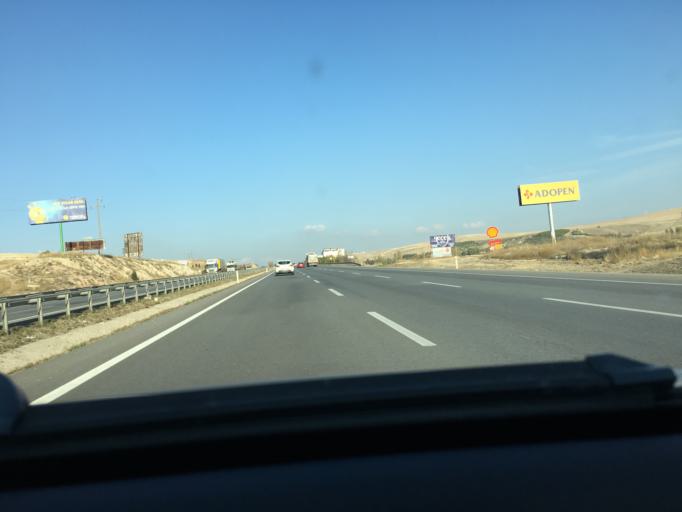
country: TR
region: Ankara
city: Temelli
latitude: 39.7842
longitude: 32.5141
